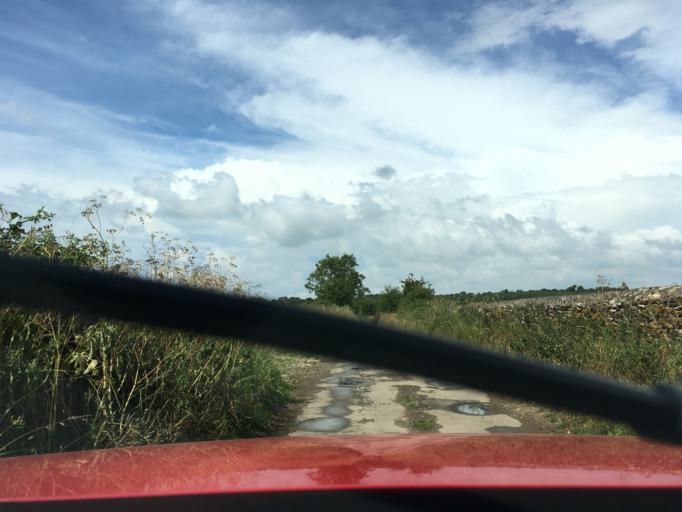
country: GB
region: England
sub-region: Gloucestershire
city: Tetbury
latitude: 51.6407
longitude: -2.1753
